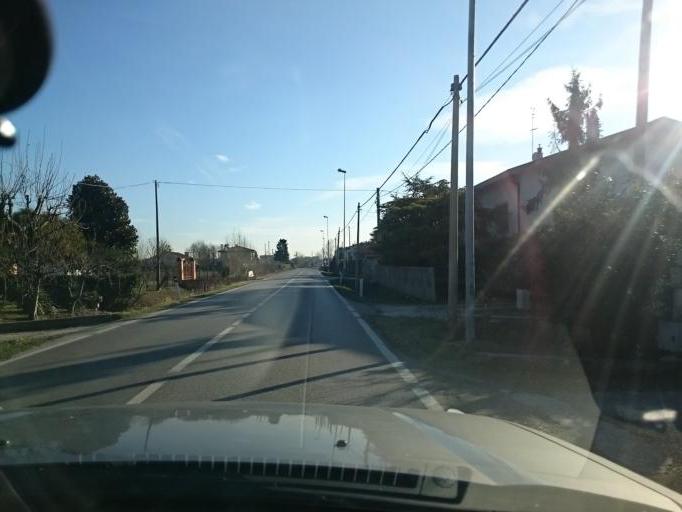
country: IT
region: Veneto
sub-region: Provincia di Padova
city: Masera di Padova
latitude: 45.3207
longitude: 11.8506
